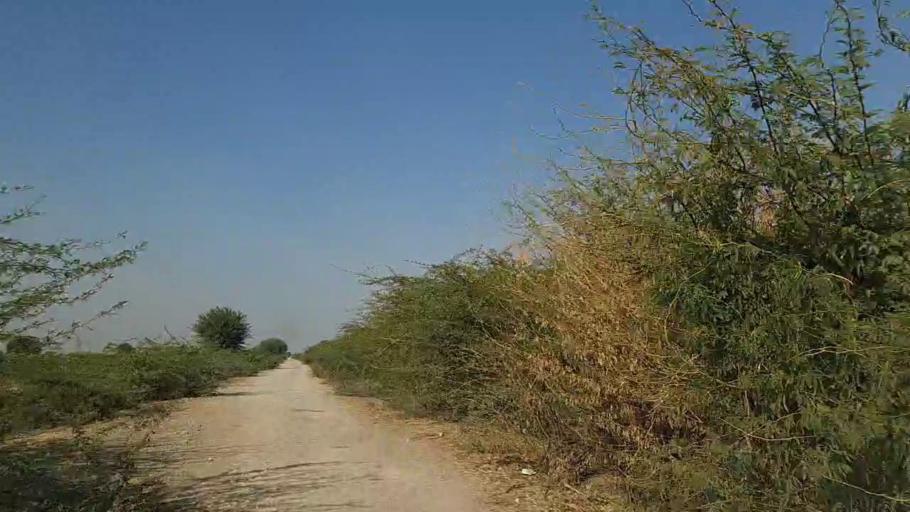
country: PK
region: Sindh
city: Naukot
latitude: 24.9319
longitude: 69.4839
